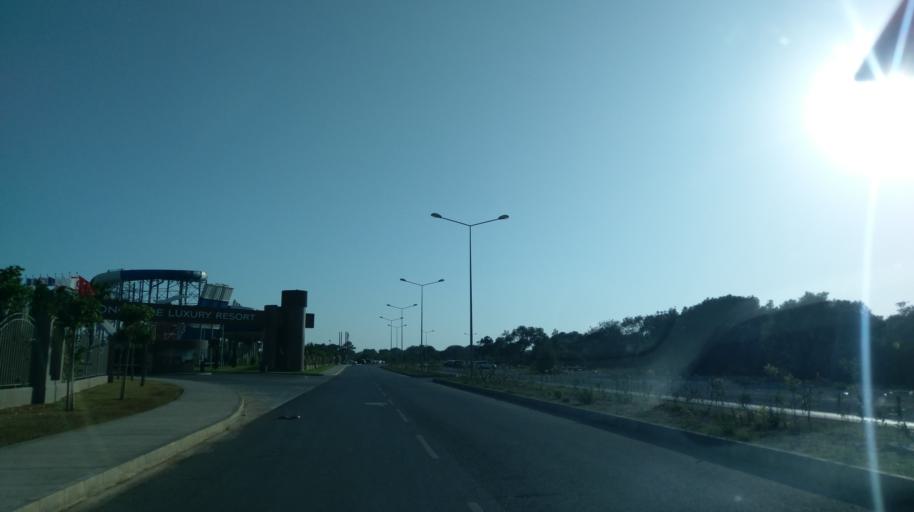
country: CY
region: Ammochostos
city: Leonarisso
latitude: 35.3565
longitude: 34.0708
